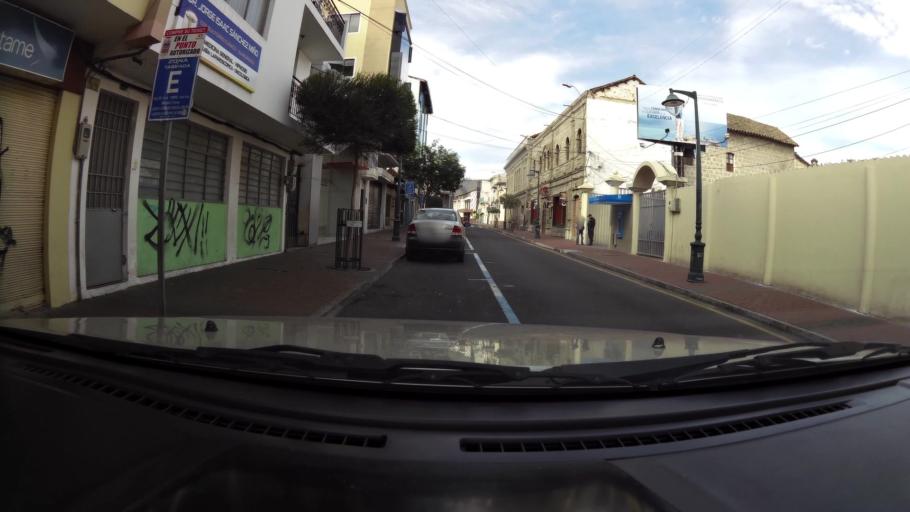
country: EC
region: Tungurahua
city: Ambato
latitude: -1.2441
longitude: -78.6304
